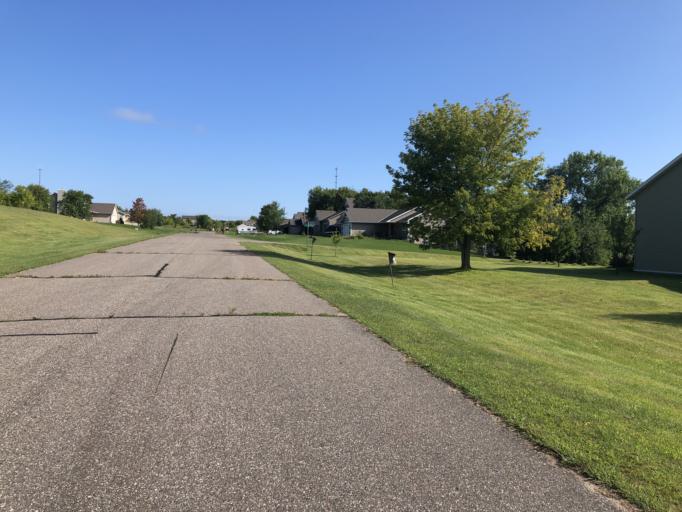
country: US
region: Minnesota
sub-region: Sherburne County
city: Becker
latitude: 45.4208
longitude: -93.8360
